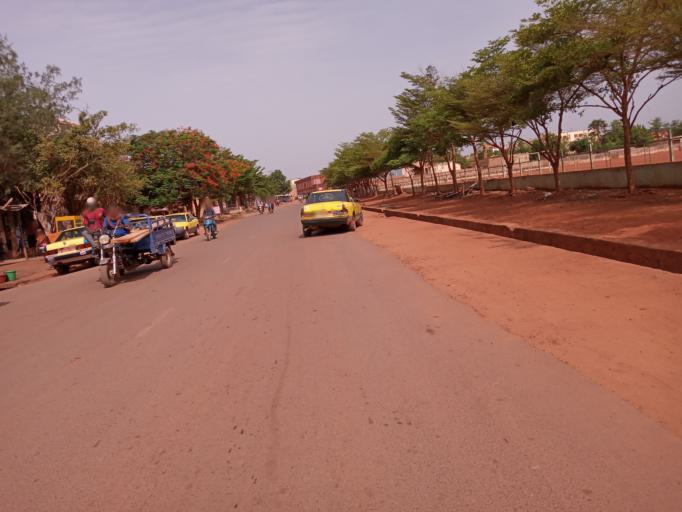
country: ML
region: Bamako
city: Bamako
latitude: 12.6099
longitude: -7.9545
